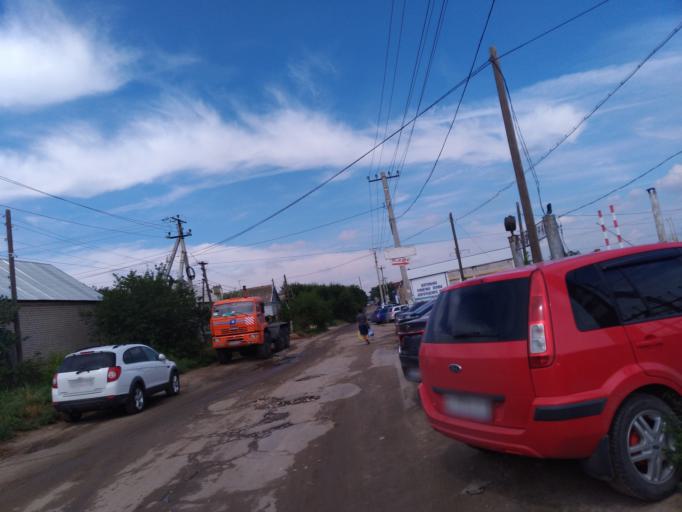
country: RU
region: Volgograd
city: Volgograd
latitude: 48.7116
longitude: 44.4619
